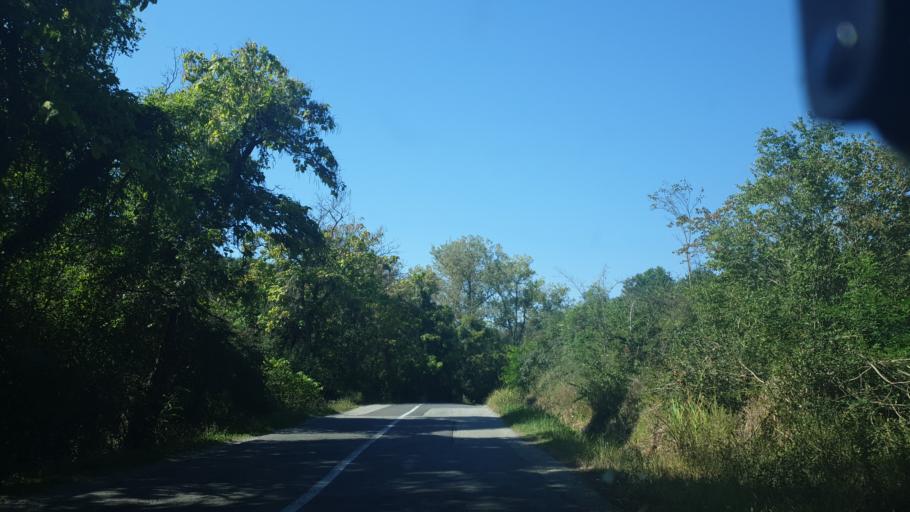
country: RS
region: Central Serbia
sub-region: Kolubarski Okrug
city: Lajkovac
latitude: 44.3204
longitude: 20.1865
